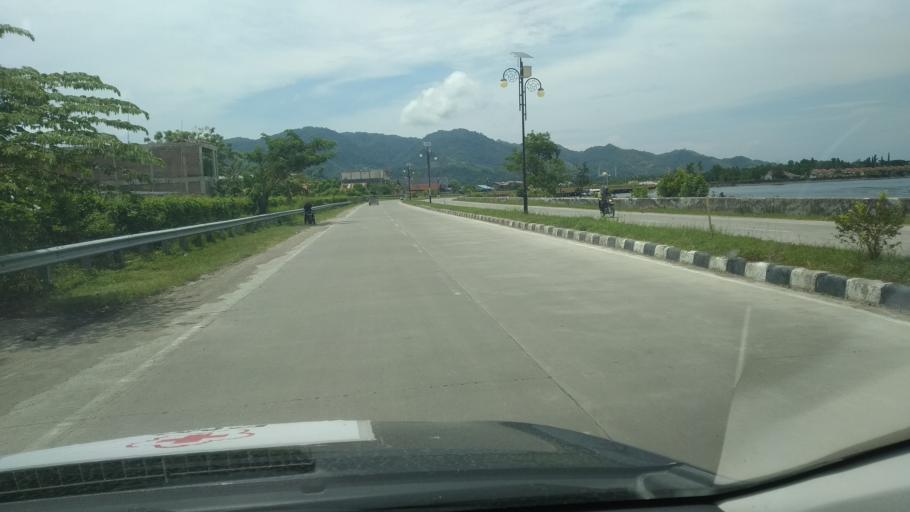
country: ID
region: Sulawesi Barat
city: Mamuju
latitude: -2.6804
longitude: 118.8703
